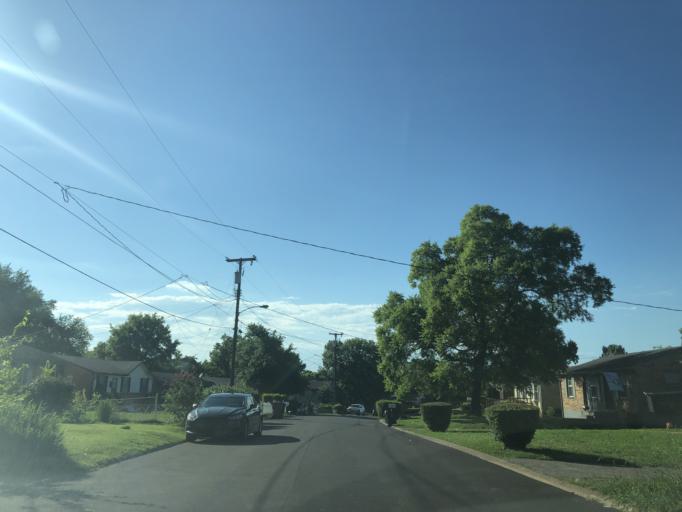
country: US
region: Tennessee
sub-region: Davidson County
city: Nashville
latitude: 36.1848
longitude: -86.8456
